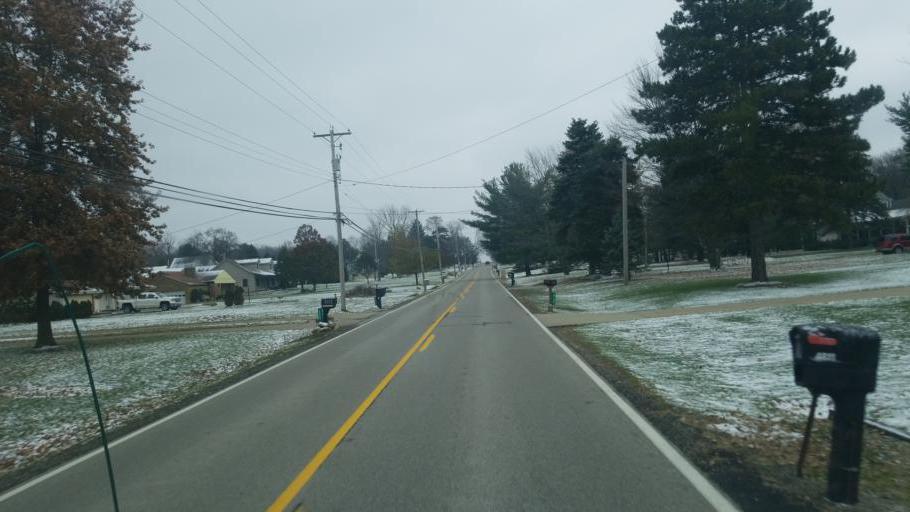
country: US
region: Ohio
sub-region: Cuyahoga County
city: North Royalton
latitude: 41.2807
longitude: -81.7188
